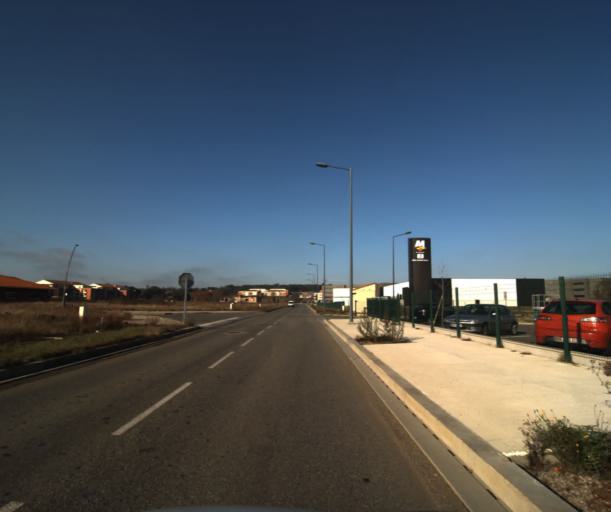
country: FR
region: Midi-Pyrenees
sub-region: Departement de la Haute-Garonne
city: Colomiers
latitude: 43.5959
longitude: 1.3538
